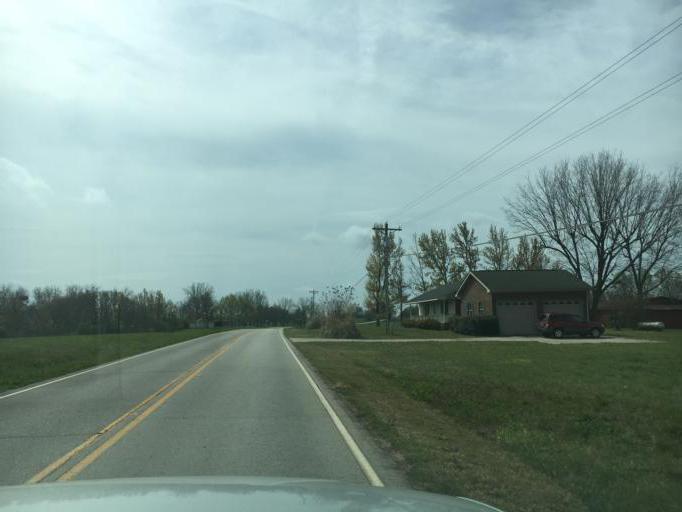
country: US
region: Georgia
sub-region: Hart County
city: Royston
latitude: 34.3390
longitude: -83.0391
